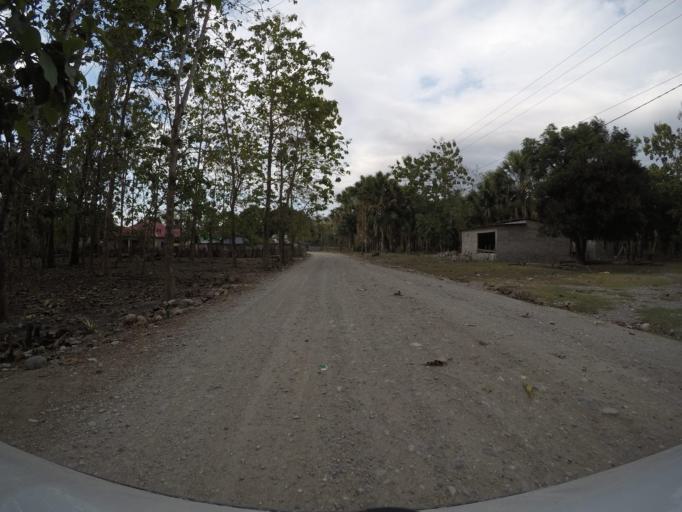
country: TL
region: Bobonaro
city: Maliana
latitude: -8.8788
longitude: 125.2121
